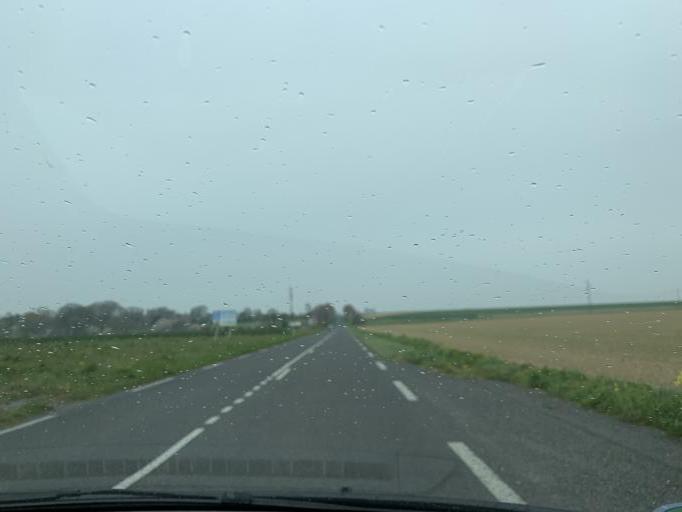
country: FR
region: Haute-Normandie
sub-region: Departement de la Seine-Maritime
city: Cany-Barville
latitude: 49.8041
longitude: 0.6665
